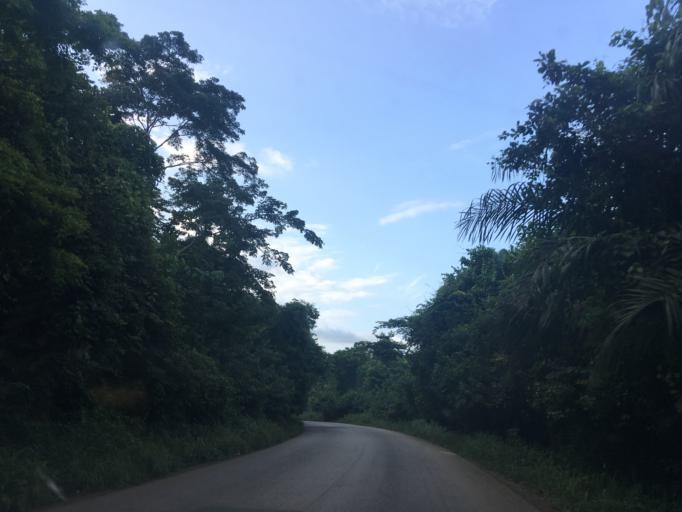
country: GH
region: Western
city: Bibiani
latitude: 6.2784
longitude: -2.2254
